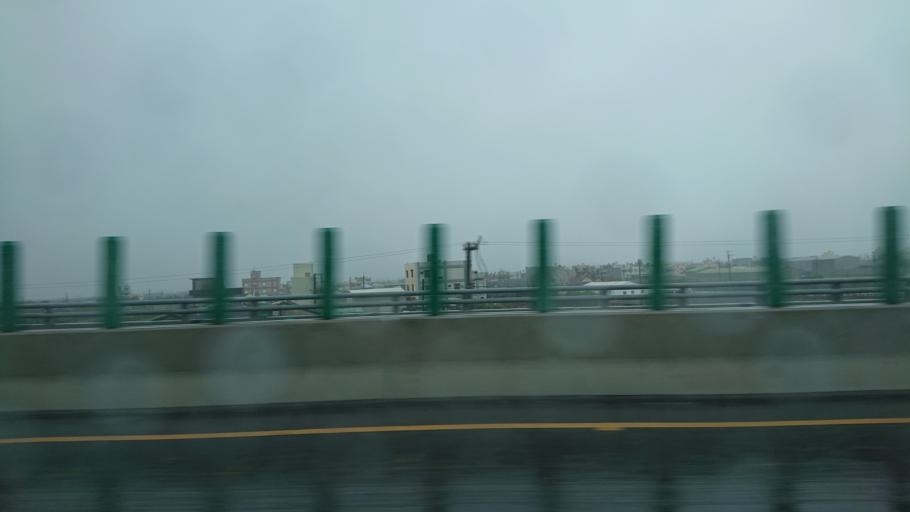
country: TW
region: Taiwan
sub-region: Changhua
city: Chang-hua
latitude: 23.9452
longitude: 120.3255
